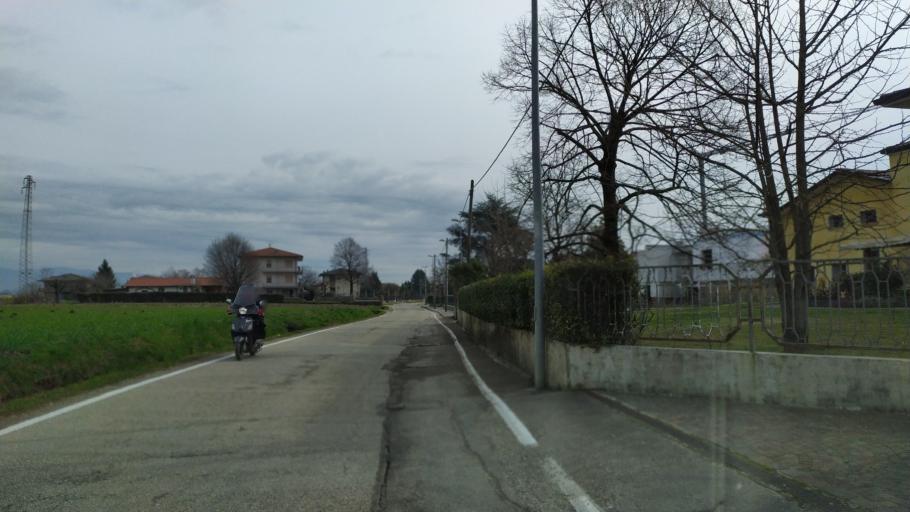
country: IT
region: Veneto
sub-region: Provincia di Vicenza
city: Malo
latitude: 45.6546
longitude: 11.4207
